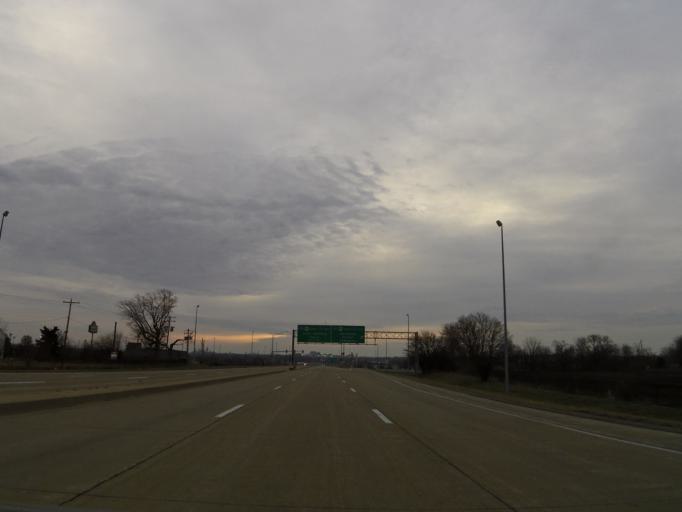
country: US
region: Illinois
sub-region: McLean County
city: Bloomington
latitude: 40.4857
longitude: -89.0340
